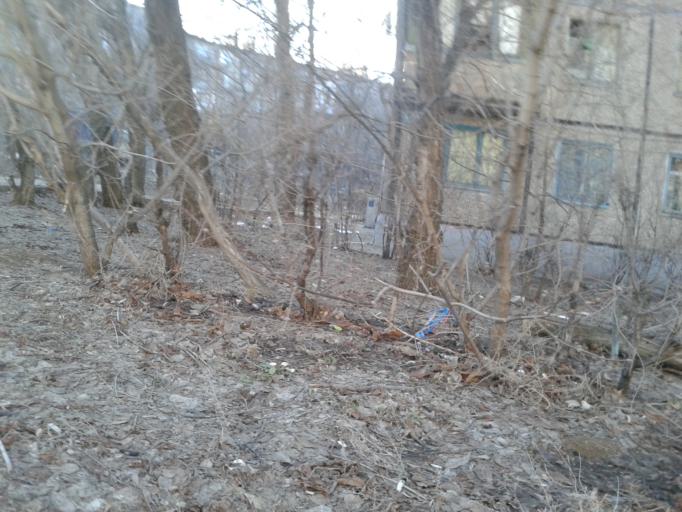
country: RU
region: Volgograd
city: Gorodishche
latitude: 48.7619
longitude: 44.4803
